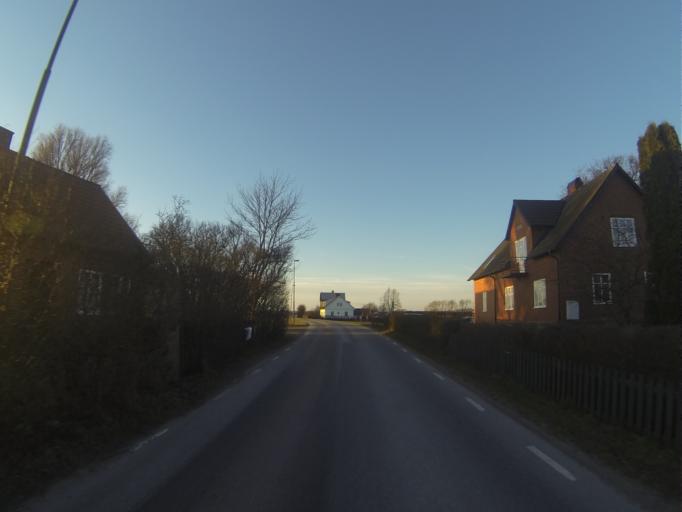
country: SE
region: Skane
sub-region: Svedala Kommun
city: Klagerup
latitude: 55.6488
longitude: 13.2662
